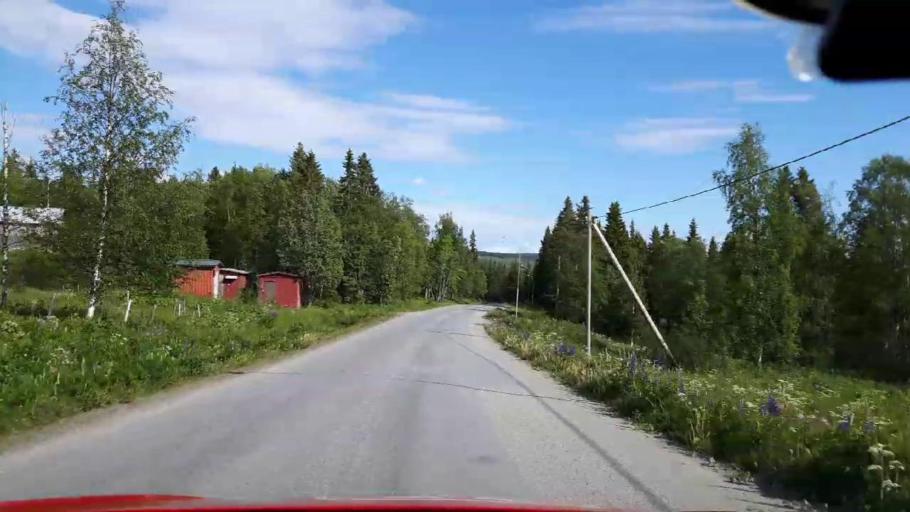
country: SE
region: Jaemtland
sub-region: Krokoms Kommun
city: Valla
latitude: 63.7642
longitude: 14.0825
